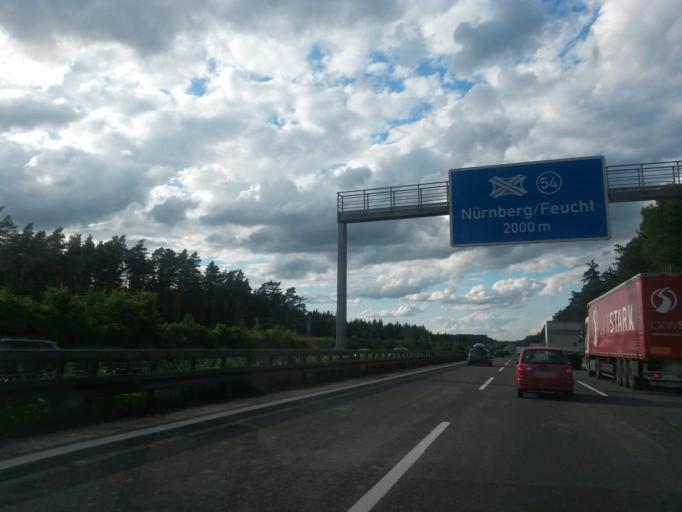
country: DE
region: Bavaria
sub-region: Regierungsbezirk Mittelfranken
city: Schwarzenbruck
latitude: 49.3223
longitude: 11.2066
